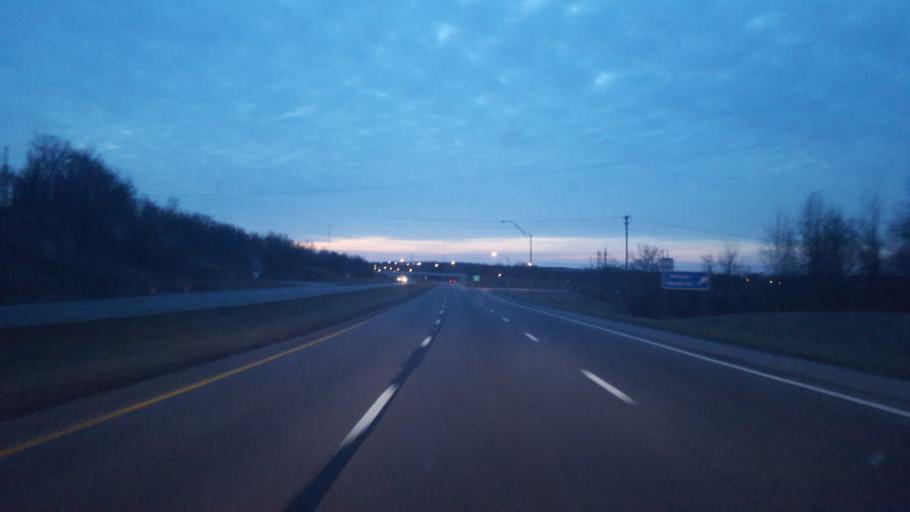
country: US
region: Ohio
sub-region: Jackson County
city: Jackson
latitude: 39.0497
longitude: -82.6173
